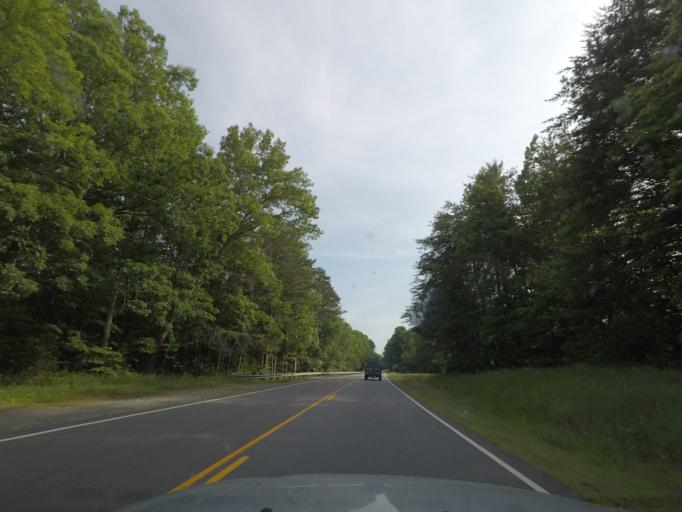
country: US
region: Virginia
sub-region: Mecklenburg County
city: Chase City
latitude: 36.8062
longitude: -78.6019
